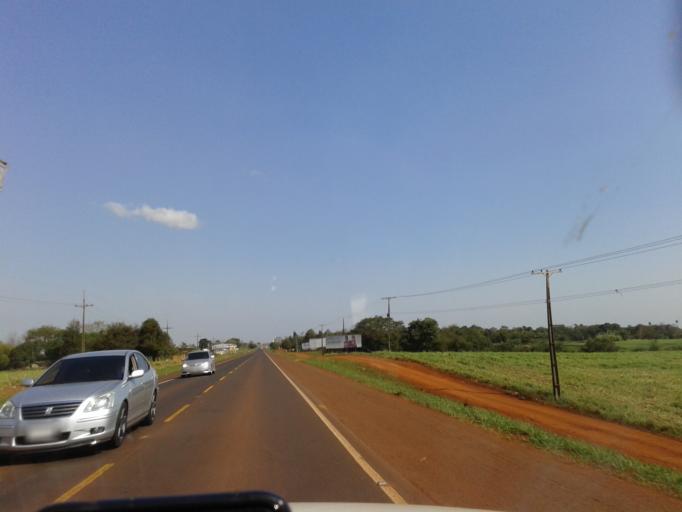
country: PY
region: Alto Parana
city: Santa Rita
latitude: -25.6801
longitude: -55.0056
